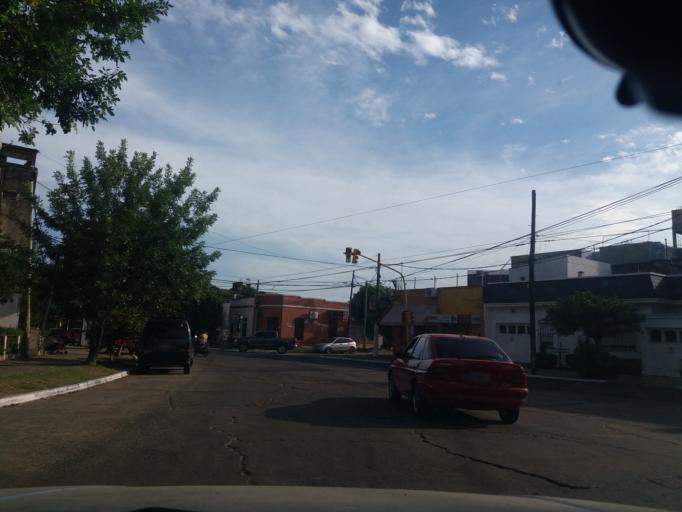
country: AR
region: Corrientes
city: Corrientes
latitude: -27.4843
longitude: -58.8322
